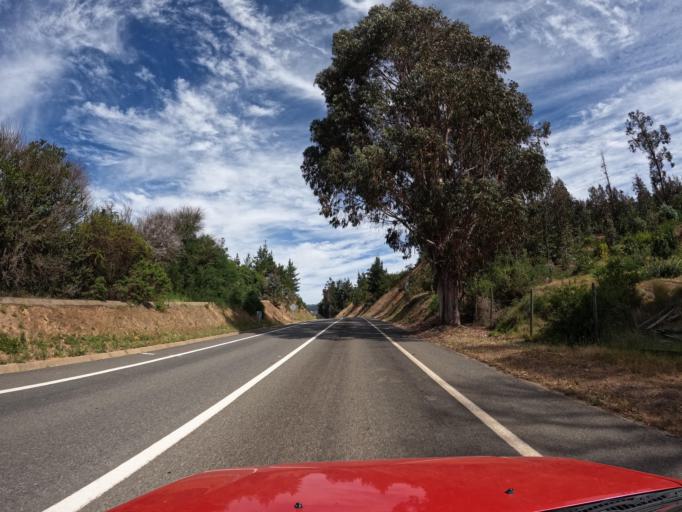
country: CL
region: Maule
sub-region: Provincia de Talca
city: Talca
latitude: -35.1511
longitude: -71.9624
